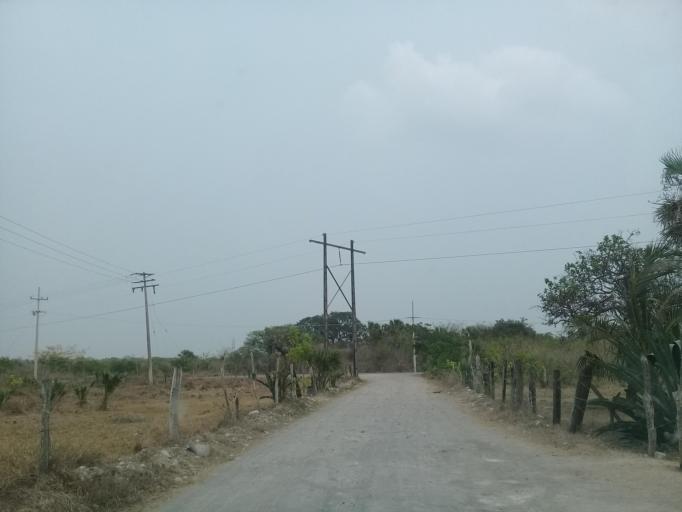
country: MX
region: Veracruz
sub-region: Medellin
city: La Laguna y Monte del Castillo
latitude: 18.9041
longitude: -96.1244
